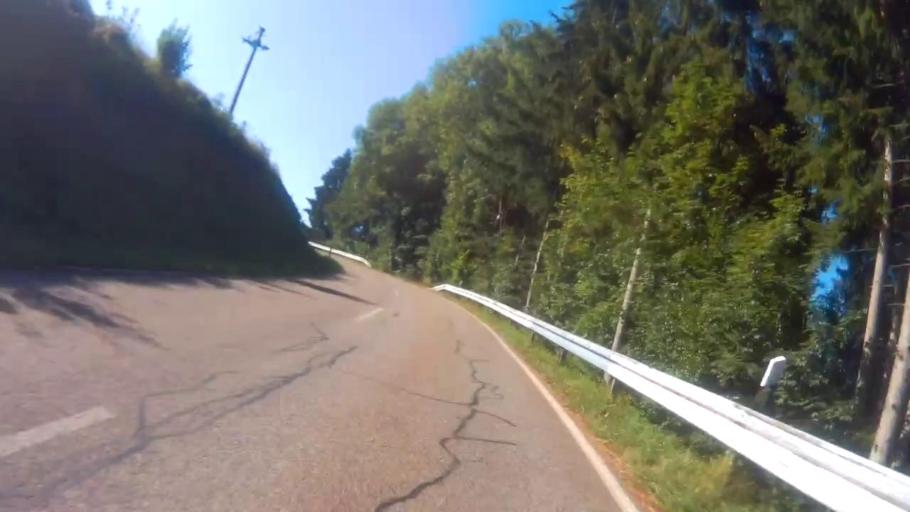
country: DE
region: Baden-Wuerttemberg
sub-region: Freiburg Region
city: Wembach
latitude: 47.7657
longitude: 7.8893
